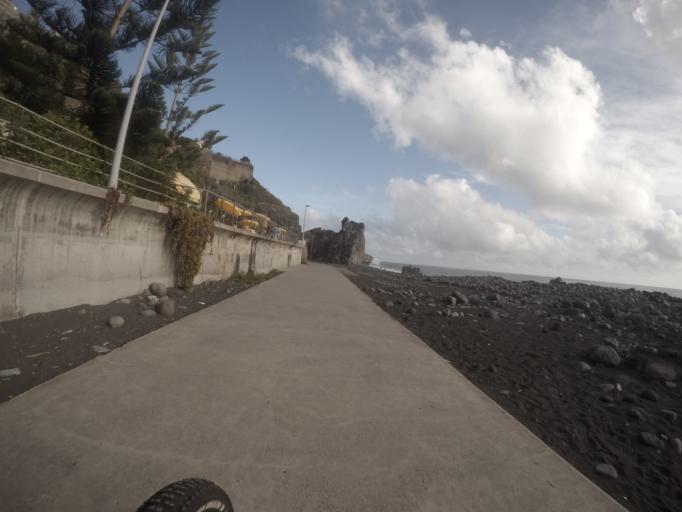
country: PT
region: Madeira
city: Camara de Lobos
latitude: 32.6430
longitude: -16.9595
